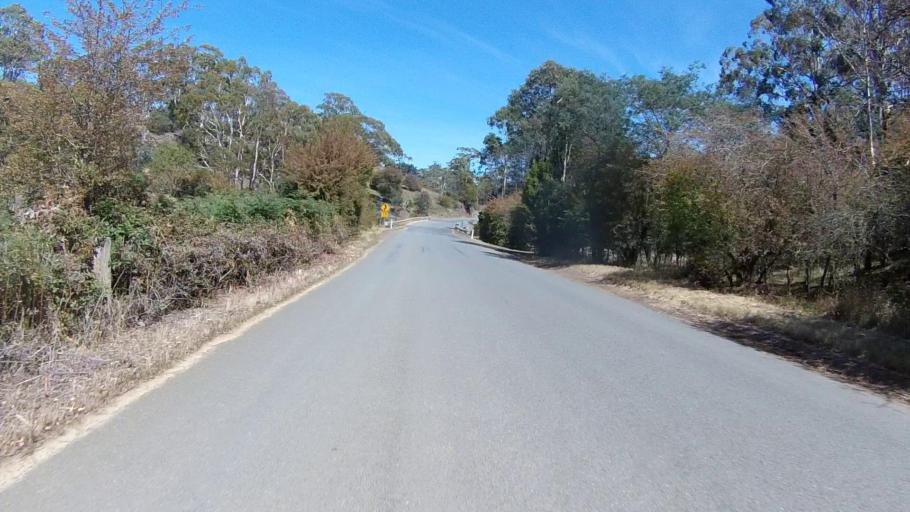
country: AU
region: Tasmania
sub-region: Sorell
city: Sorell
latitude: -42.7586
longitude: 147.6555
